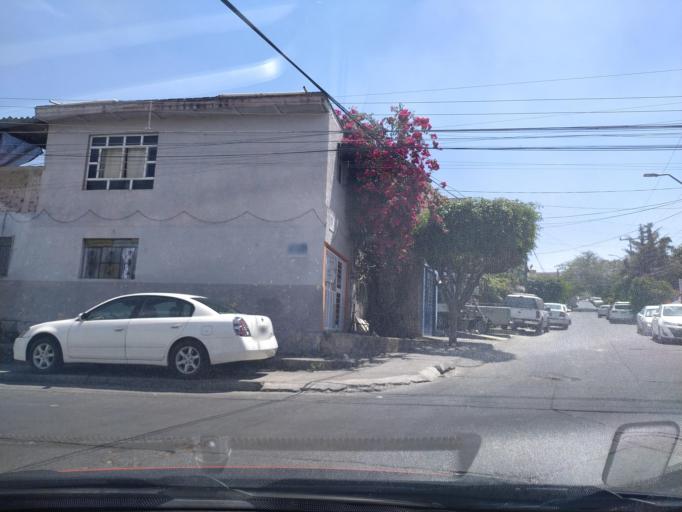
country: MX
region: Jalisco
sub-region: Tlajomulco de Zuniga
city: Altus Bosques
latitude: 20.6149
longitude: -103.3704
